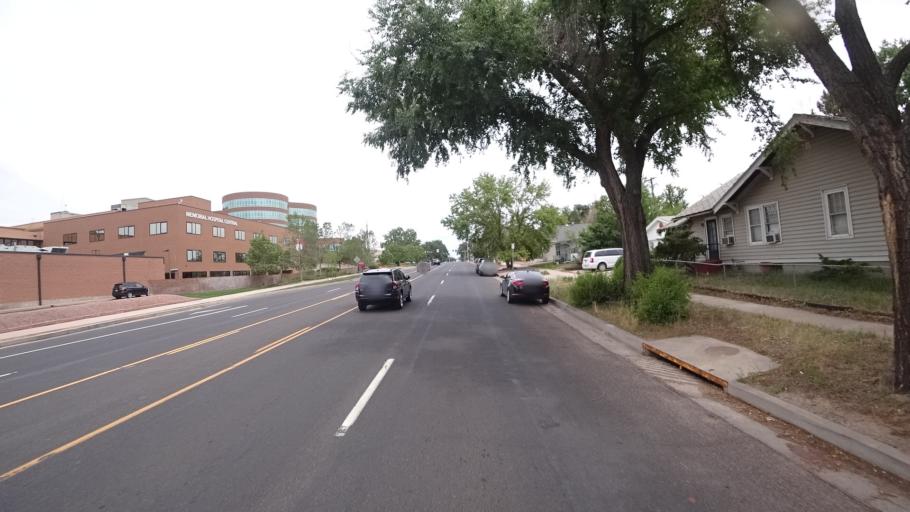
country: US
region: Colorado
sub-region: El Paso County
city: Colorado Springs
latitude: 38.8388
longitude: -104.8004
